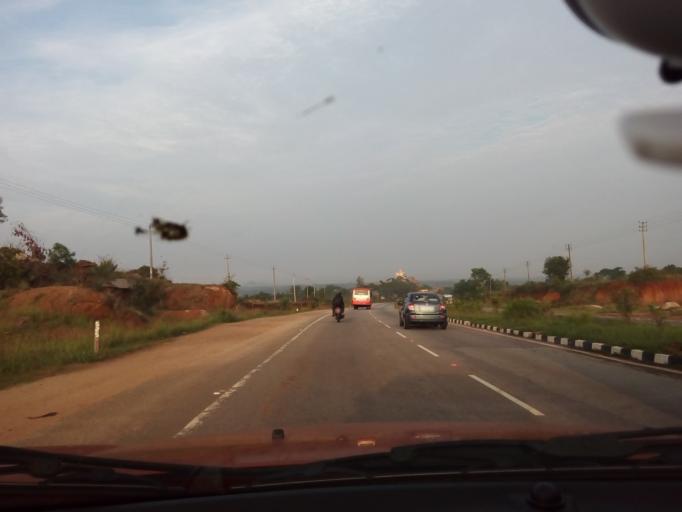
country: IN
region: Karnataka
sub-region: Bangalore Rural
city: Nelamangala
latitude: 13.0642
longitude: 77.2816
